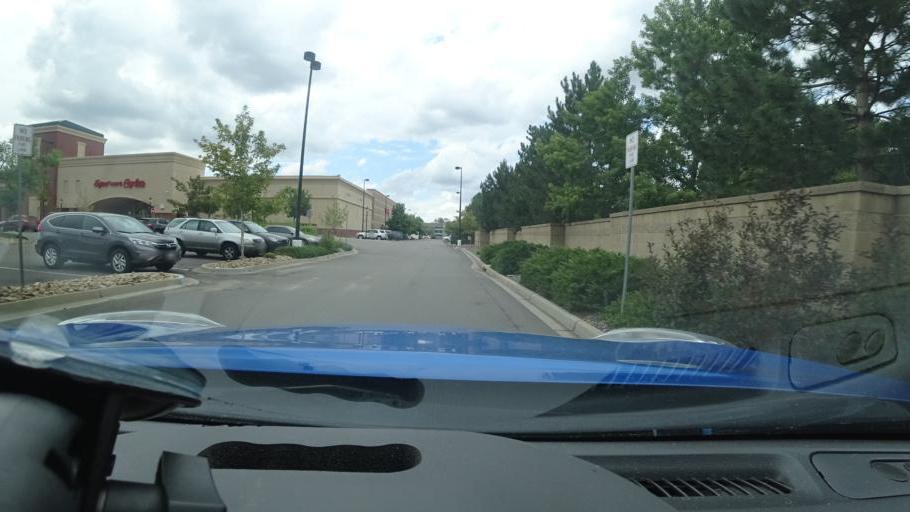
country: US
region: Colorado
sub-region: Adams County
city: Aurora
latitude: 39.7149
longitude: -104.8206
